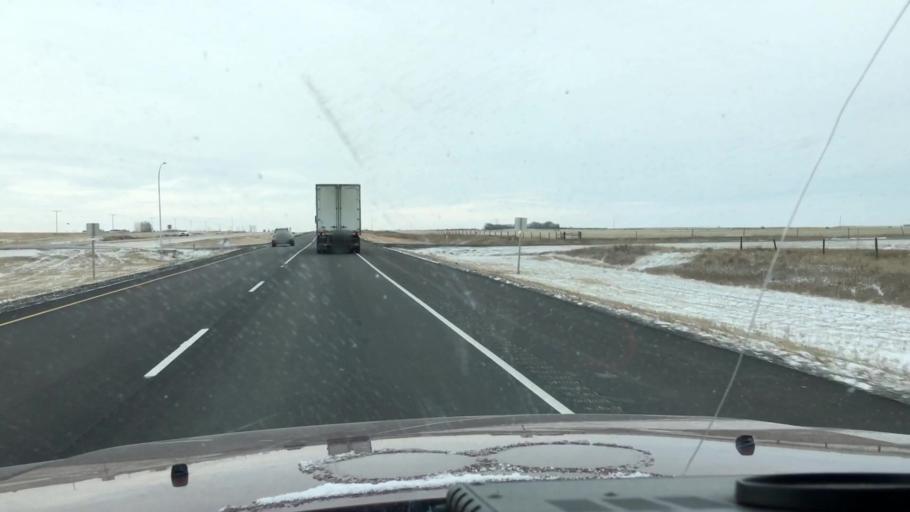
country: CA
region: Saskatchewan
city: Saskatoon
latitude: 51.7952
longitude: -106.4865
